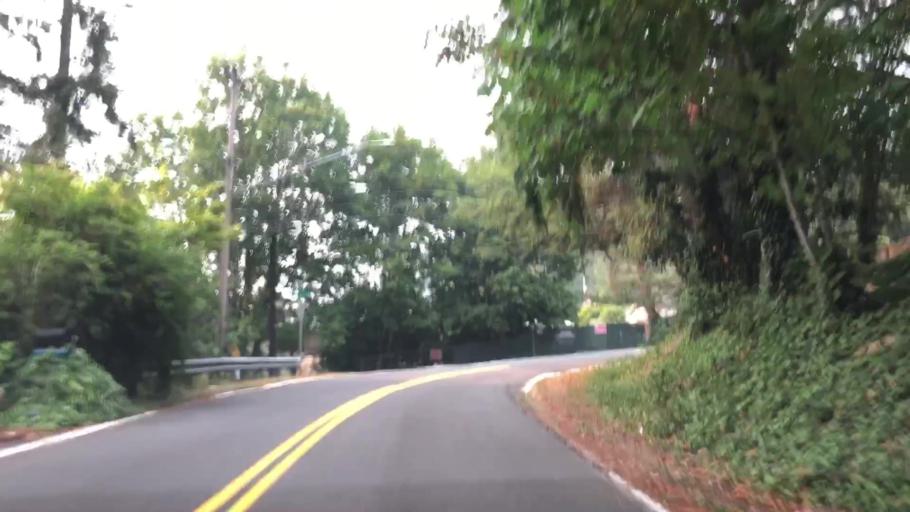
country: US
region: Washington
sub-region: King County
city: Kenmore
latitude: 47.7802
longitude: -122.2430
